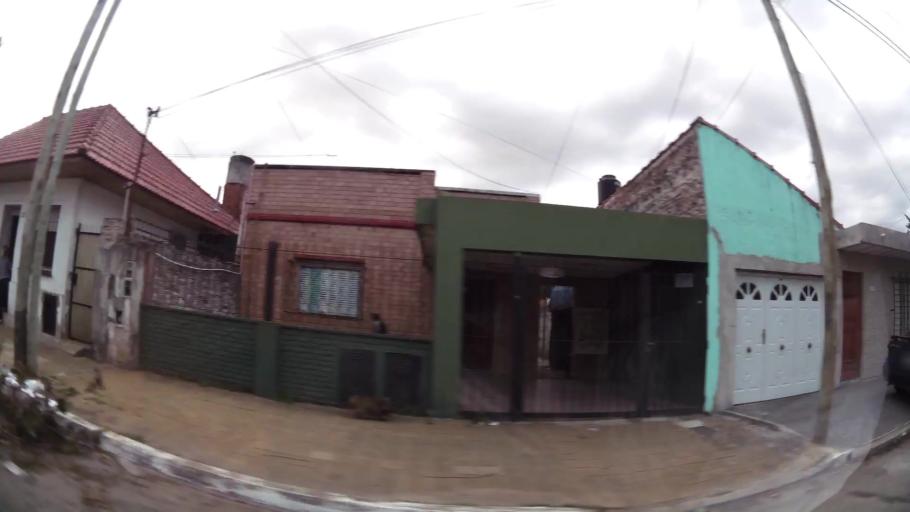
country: AR
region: Buenos Aires
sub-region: Partido de Quilmes
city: Quilmes
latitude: -34.7492
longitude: -58.2334
